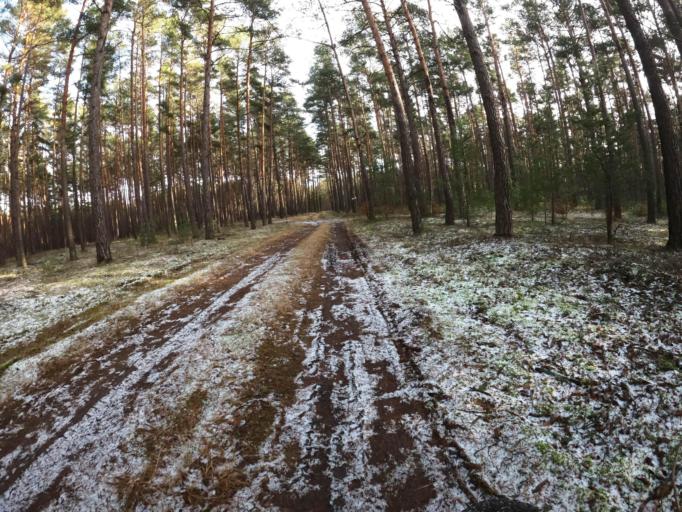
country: PL
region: Lubusz
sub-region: Powiat slubicki
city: Cybinka
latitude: 52.2435
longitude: 14.8158
